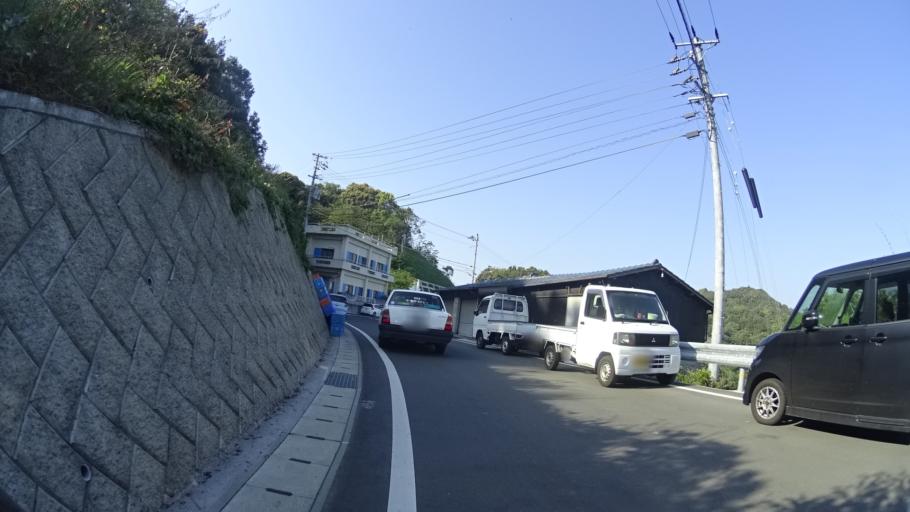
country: JP
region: Oita
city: Tsukumiura
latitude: 33.3495
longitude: 132.0279
